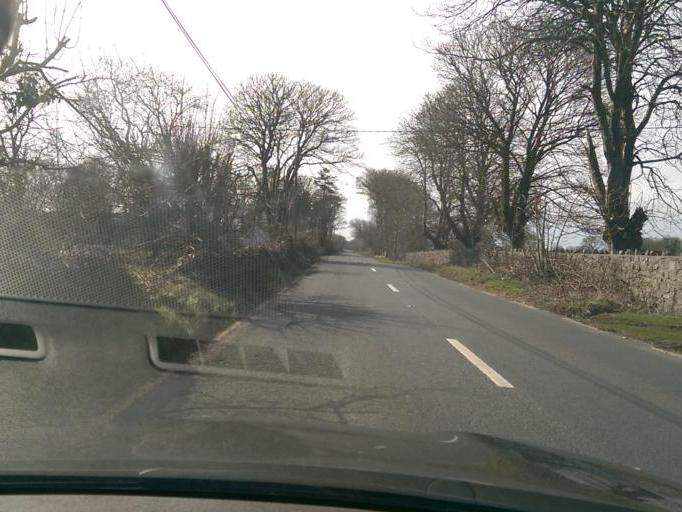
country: IE
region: Connaught
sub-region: County Galway
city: Athenry
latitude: 53.4506
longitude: -8.7037
